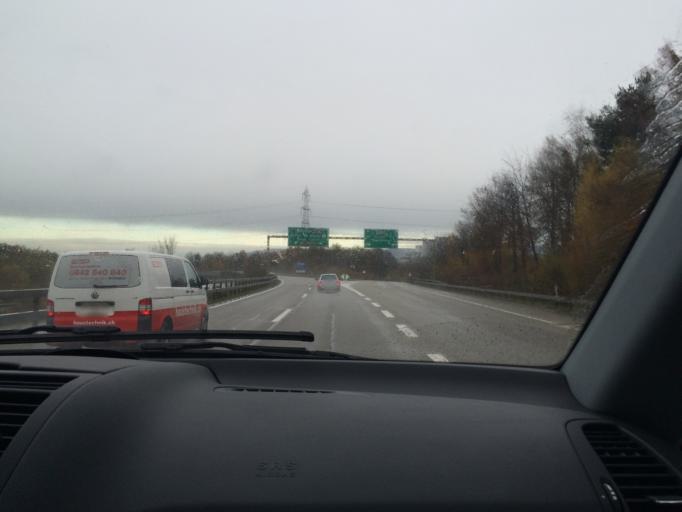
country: CH
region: Aargau
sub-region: Bezirk Rheinfelden
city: Kaiseraugst
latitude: 47.5288
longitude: 7.7378
